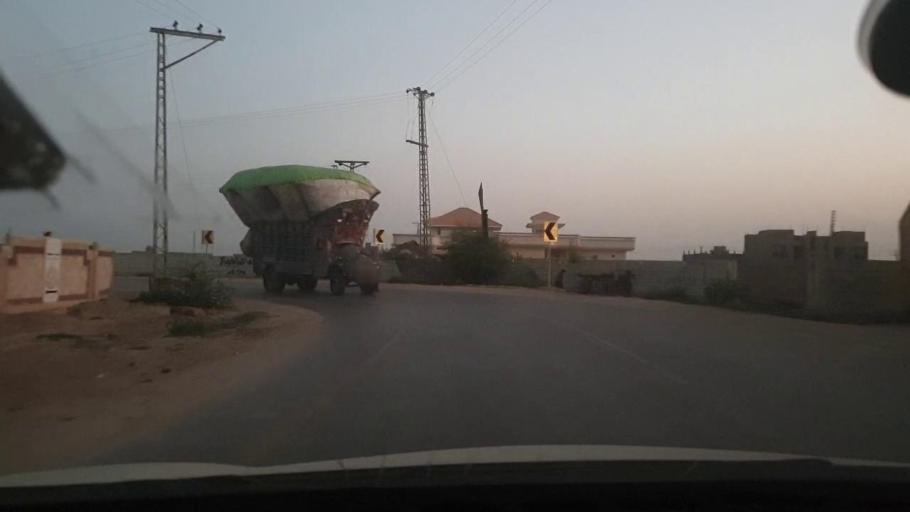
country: PK
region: Sindh
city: Tando Adam
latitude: 25.7481
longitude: 68.6449
